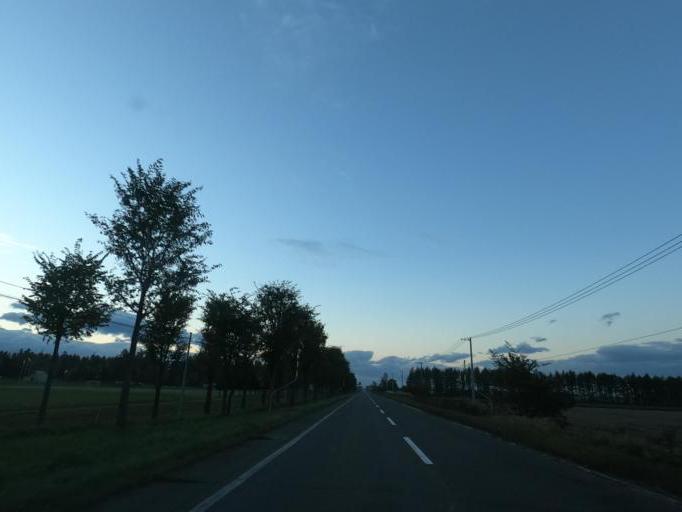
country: JP
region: Hokkaido
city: Obihiro
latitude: 42.6432
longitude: 143.2008
